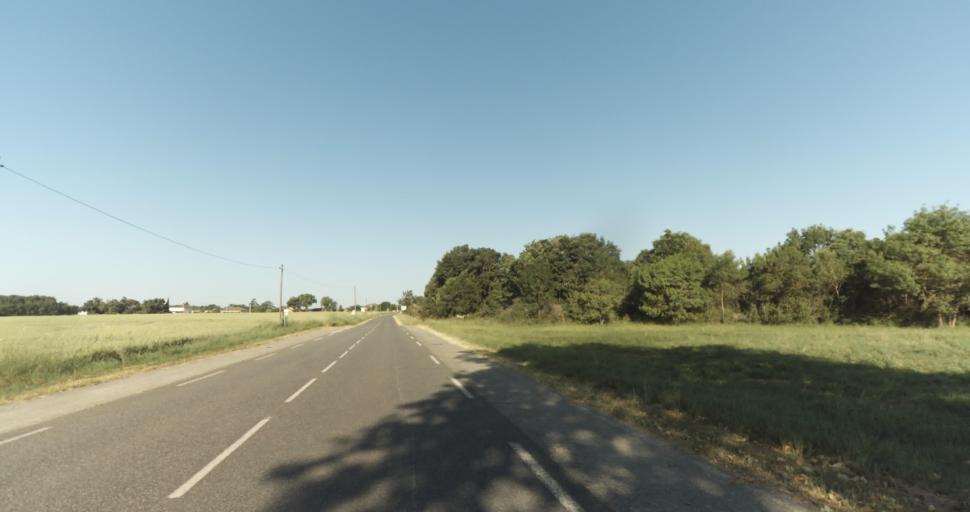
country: FR
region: Midi-Pyrenees
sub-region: Departement de la Haute-Garonne
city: Leguevin
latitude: 43.5698
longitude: 1.2374
